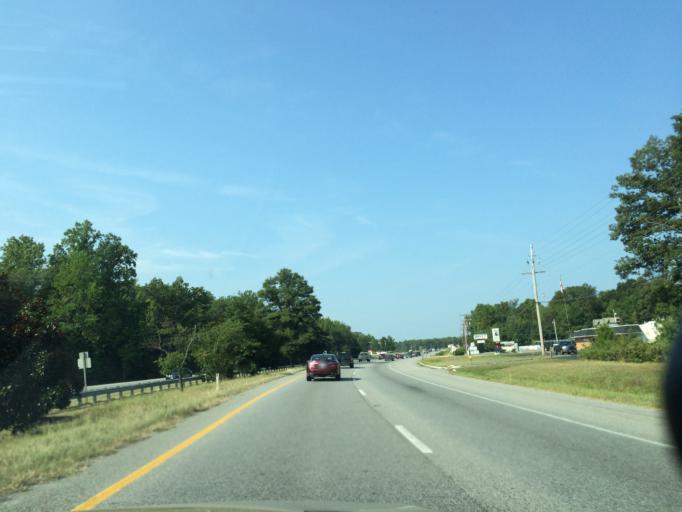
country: US
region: Maryland
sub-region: Charles County
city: Saint Charles
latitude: 38.5812
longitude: -76.9535
